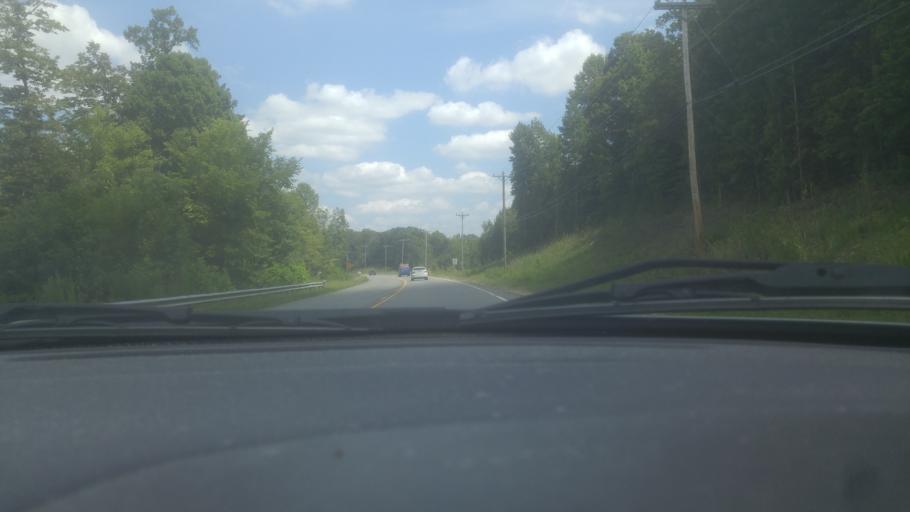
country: US
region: North Carolina
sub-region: Rowan County
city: Enochville
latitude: 35.4376
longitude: -80.7101
